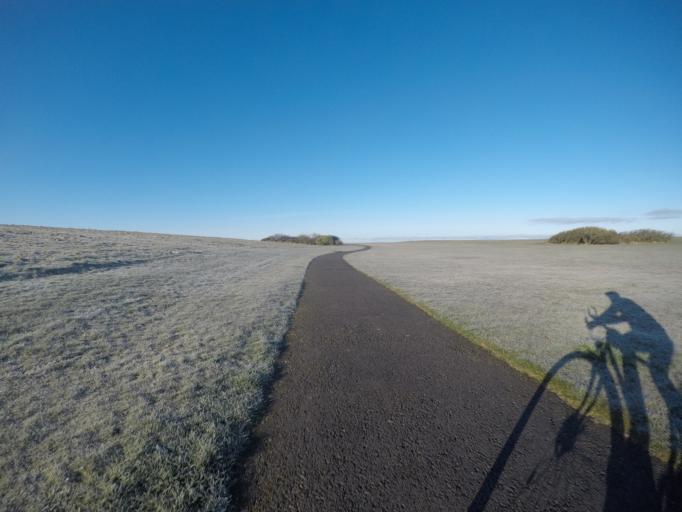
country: GB
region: Scotland
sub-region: North Ayrshire
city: Stevenston
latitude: 55.6272
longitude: -4.7443
